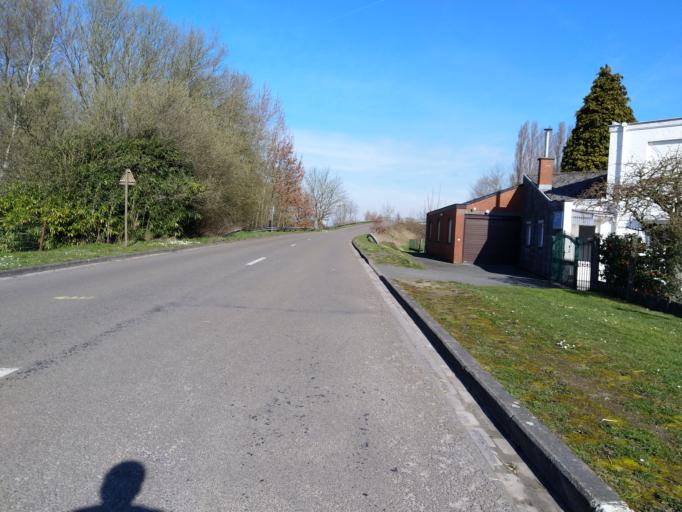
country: BE
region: Wallonia
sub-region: Province du Hainaut
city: Soignies
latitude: 50.5396
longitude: 4.0073
